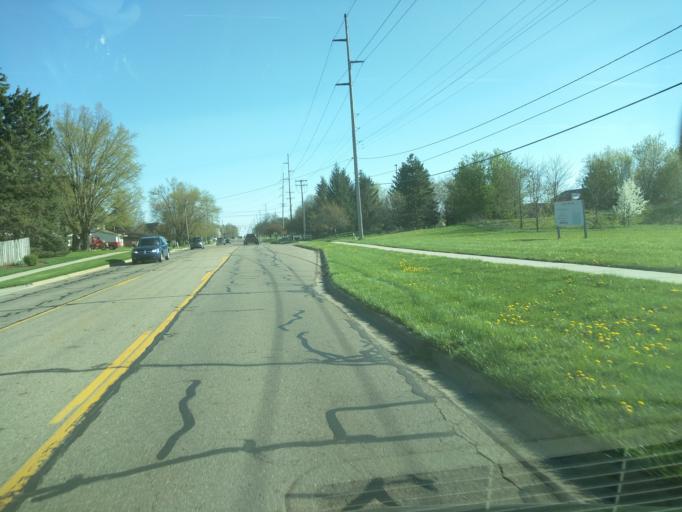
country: US
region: Michigan
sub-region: Eaton County
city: Waverly
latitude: 42.7439
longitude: -84.6423
